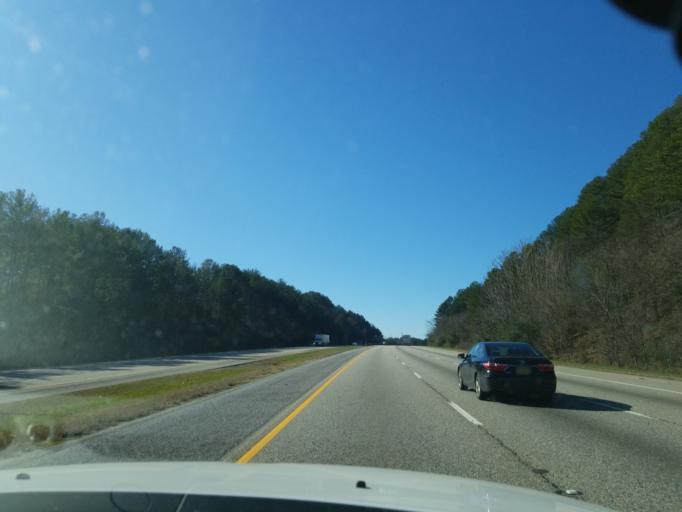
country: US
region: Alabama
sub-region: Shelby County
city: Helena
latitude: 33.3496
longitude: -86.8610
